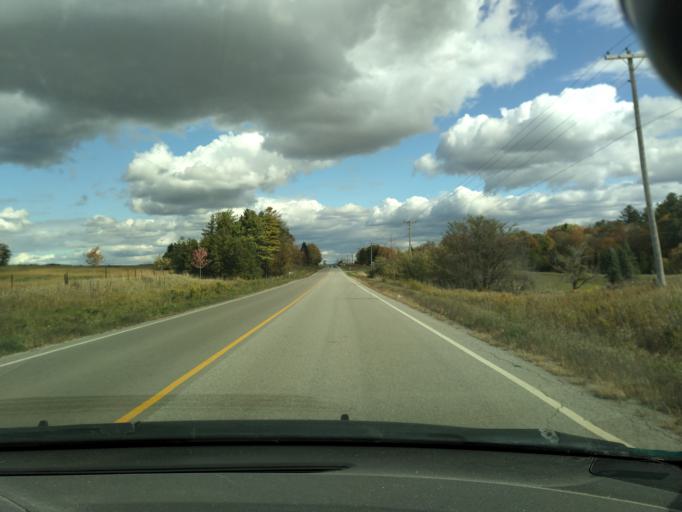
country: CA
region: Ontario
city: Bradford West Gwillimbury
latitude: 44.0825
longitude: -79.5918
